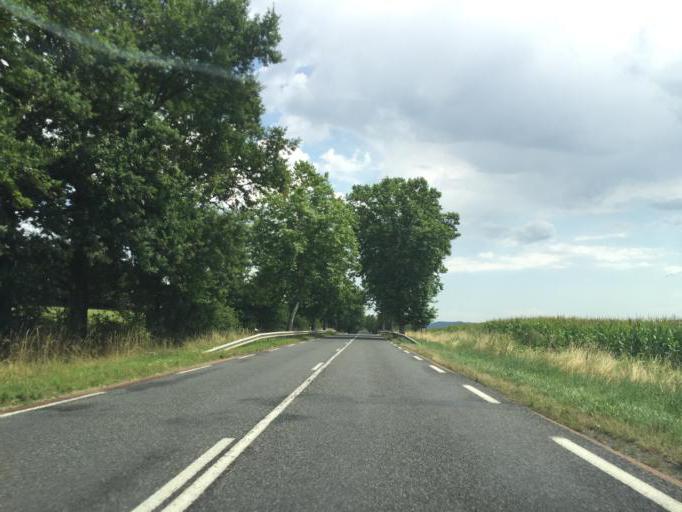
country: FR
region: Rhone-Alpes
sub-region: Departement du Rhone
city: Saint-Romain-de-Popey
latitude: 45.8720
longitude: 4.5391
